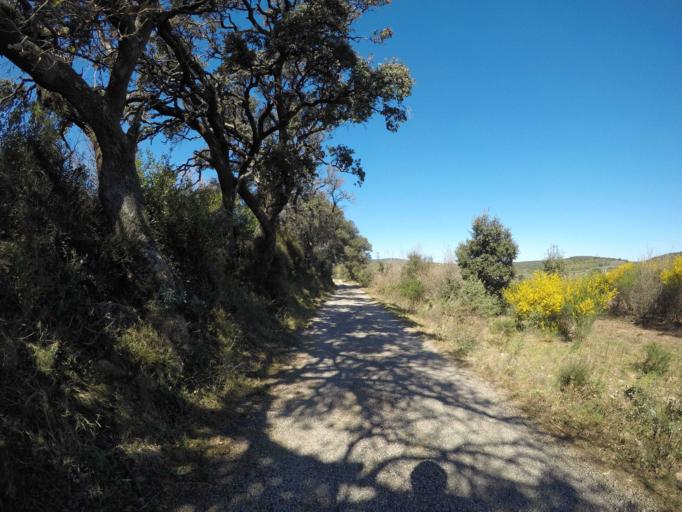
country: FR
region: Languedoc-Roussillon
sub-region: Departement des Pyrenees-Orientales
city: Millas
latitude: 42.7073
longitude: 2.6696
